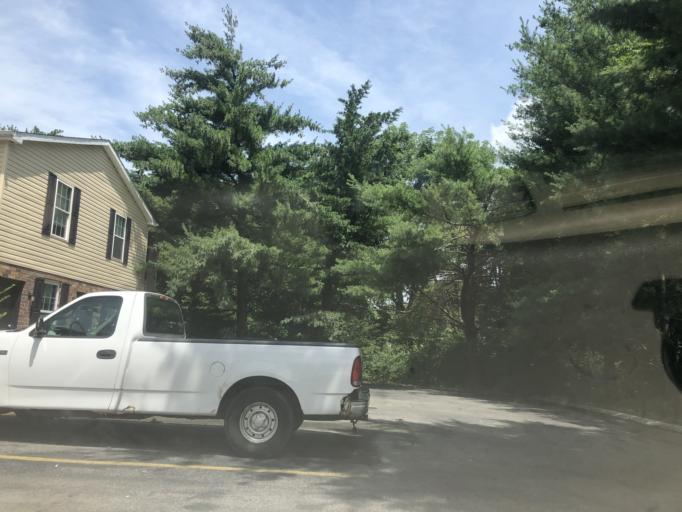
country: US
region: Tennessee
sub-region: Davidson County
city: Lakewood
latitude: 36.2581
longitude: -86.6775
